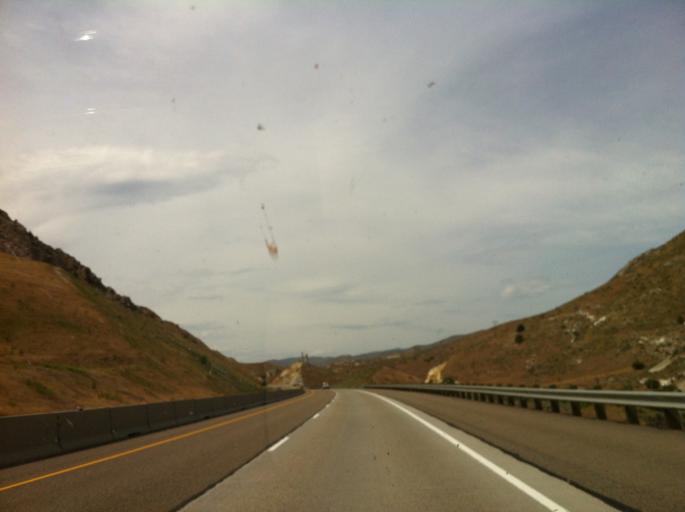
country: US
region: Idaho
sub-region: Washington County
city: Weiser
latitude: 44.3712
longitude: -117.2960
